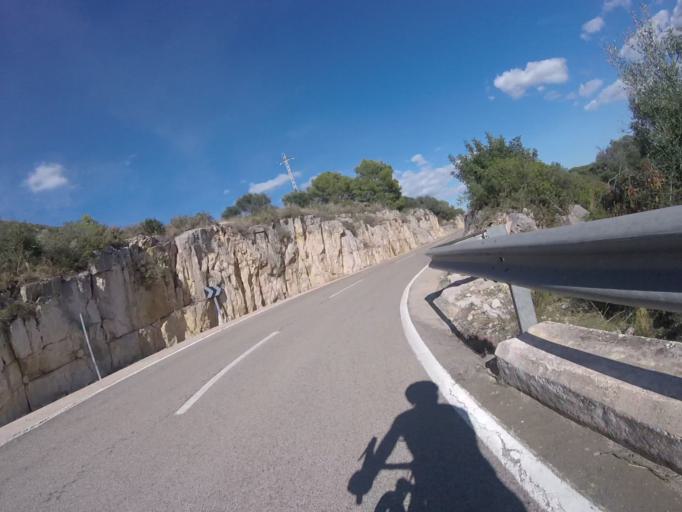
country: ES
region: Valencia
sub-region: Provincia de Castello
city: Alcala de Xivert
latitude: 40.2982
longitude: 0.1868
